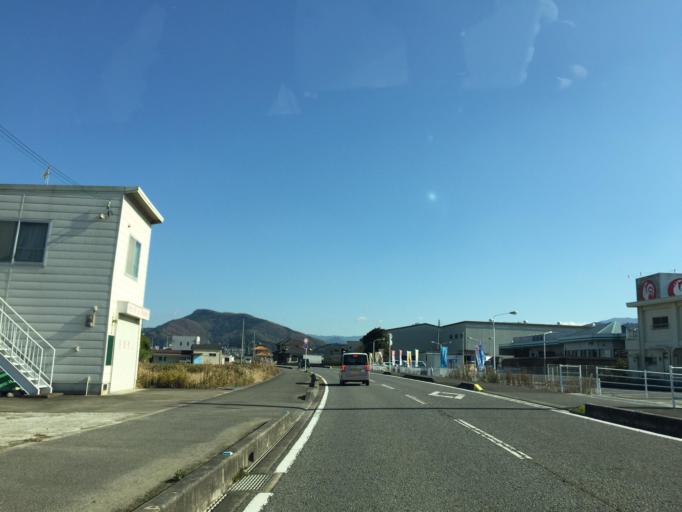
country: JP
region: Wakayama
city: Kainan
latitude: 34.1621
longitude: 135.2816
